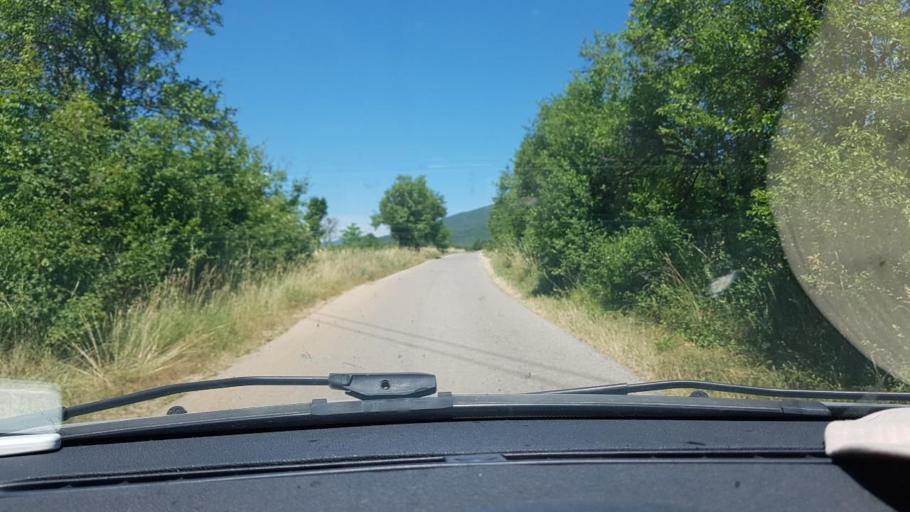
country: HR
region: Licko-Senjska
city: Otocac
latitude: 44.7953
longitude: 15.3652
